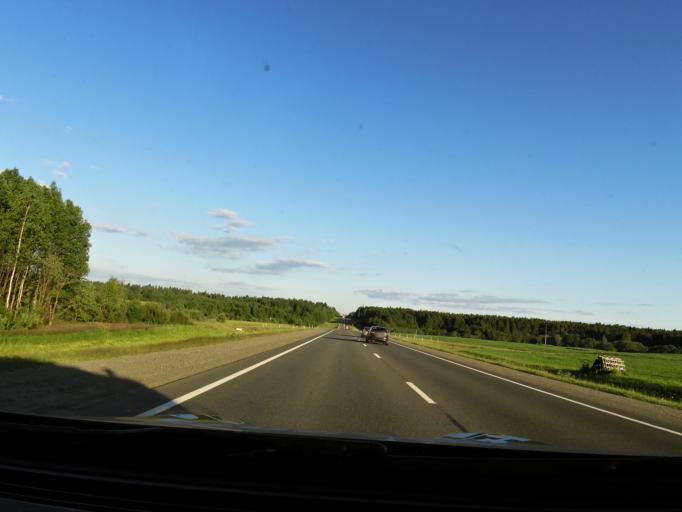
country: RU
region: Vologda
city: Vologda
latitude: 59.1401
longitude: 39.9489
